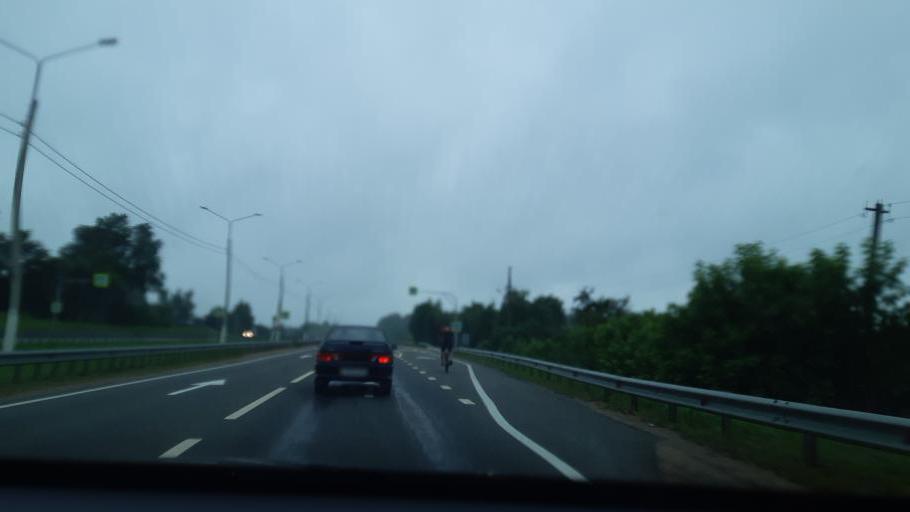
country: RU
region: Smolensk
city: Talashkino
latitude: 54.6730
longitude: 32.1478
